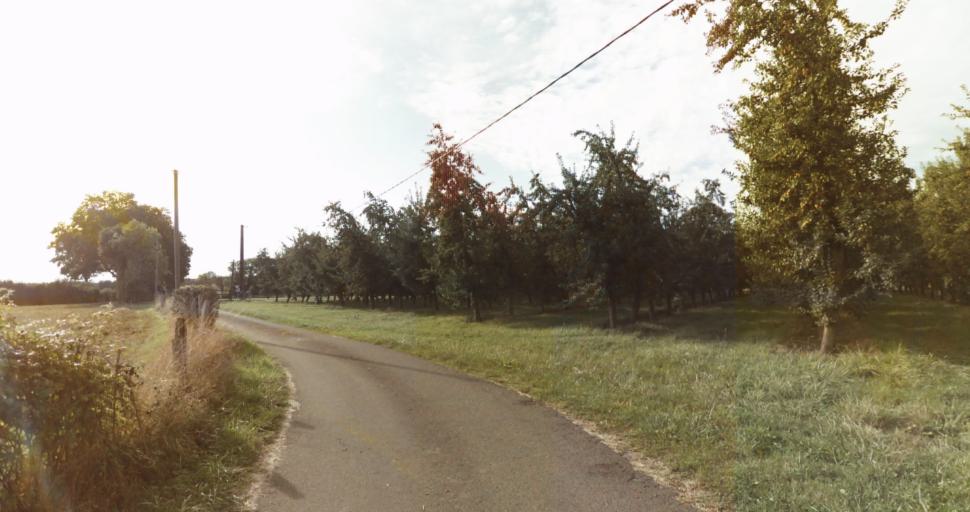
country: FR
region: Lower Normandy
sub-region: Departement de l'Orne
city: Gace
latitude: 48.6971
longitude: 0.3138
